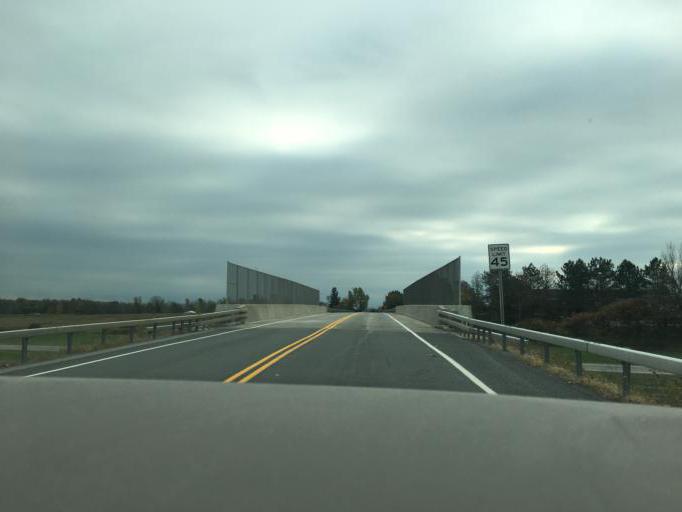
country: US
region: New York
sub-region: Wayne County
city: Macedon
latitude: 42.9918
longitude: -77.3263
